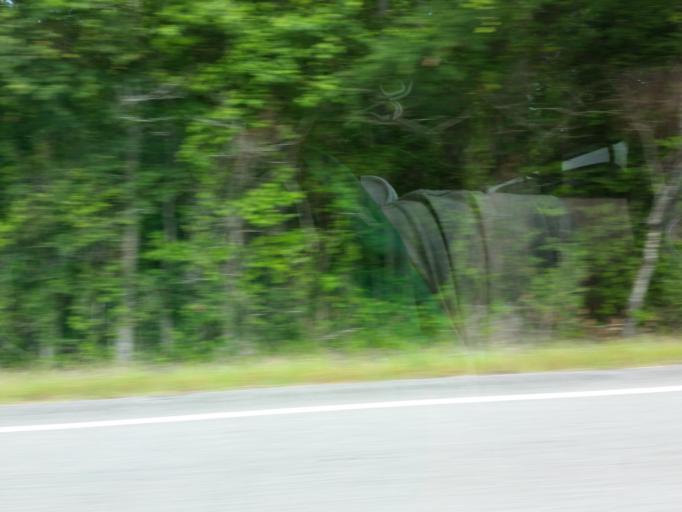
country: US
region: Alabama
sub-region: Sumter County
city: York
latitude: 32.3718
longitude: -88.1932
